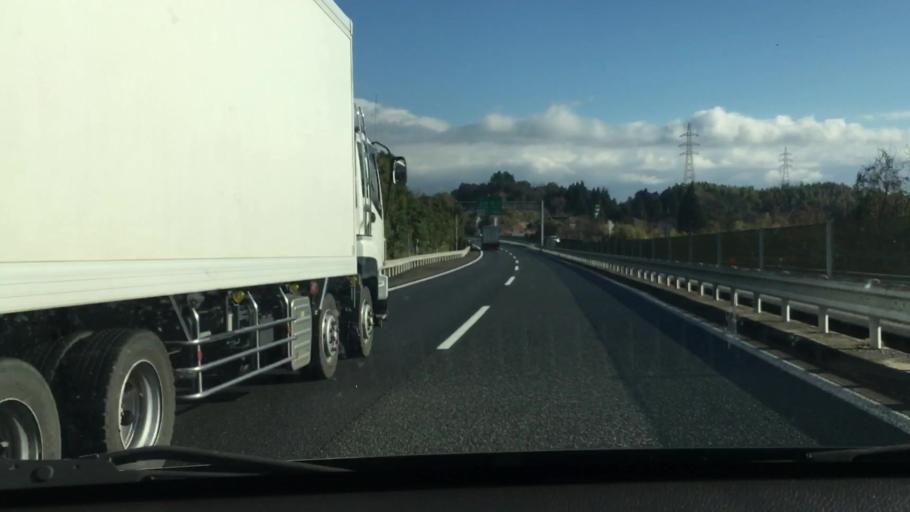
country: JP
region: Kumamoto
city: Hitoyoshi
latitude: 32.2363
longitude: 130.7636
